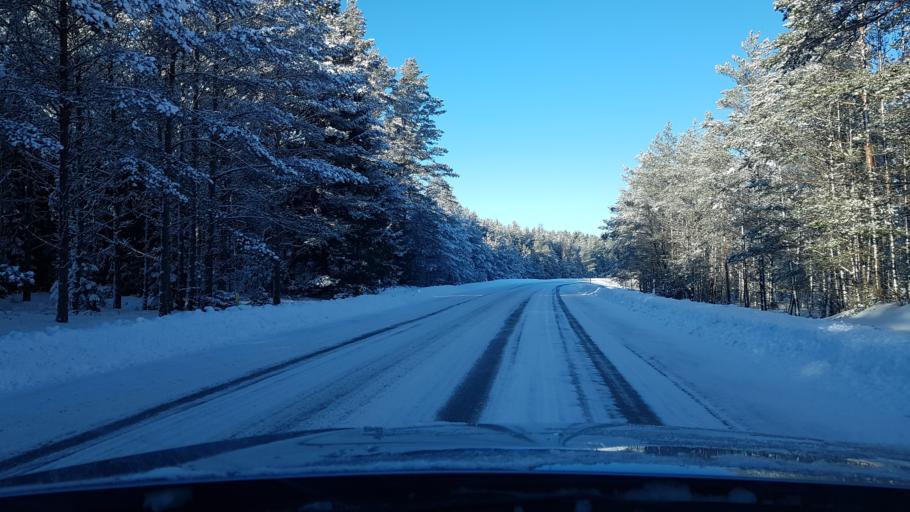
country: EE
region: Hiiumaa
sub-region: Kaerdla linn
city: Kardla
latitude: 58.9457
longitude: 22.7726
